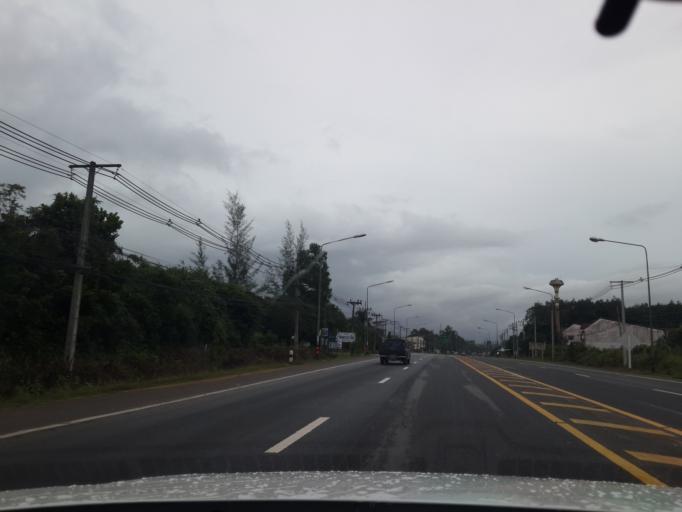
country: TH
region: Songkhla
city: Khlong Hoi Khong
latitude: 6.9452
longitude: 100.4086
